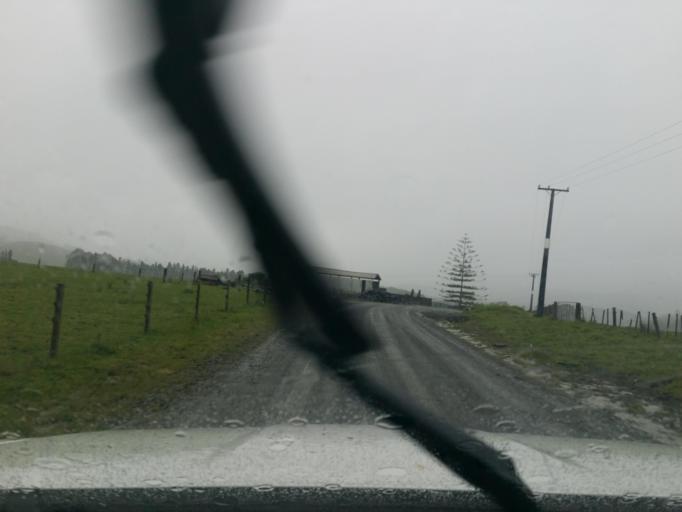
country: NZ
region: Northland
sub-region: Whangarei
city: Maungatapere
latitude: -35.8032
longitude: 174.0494
